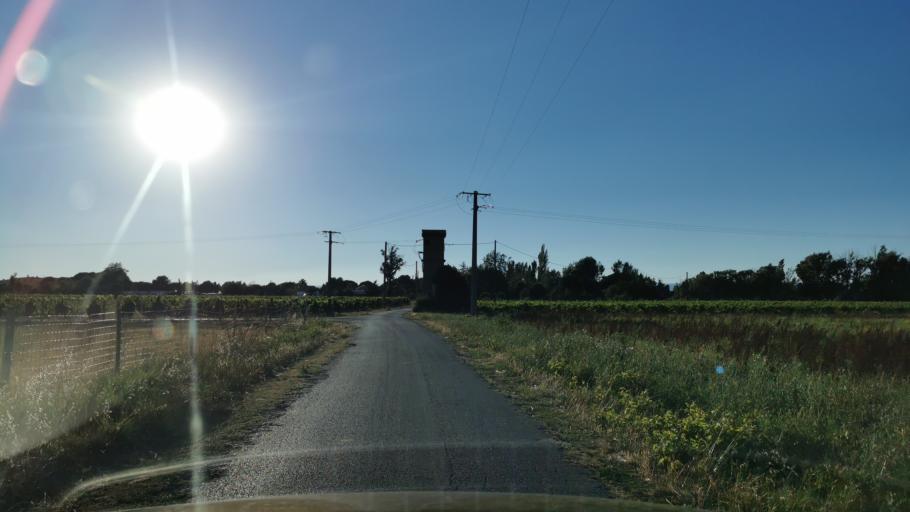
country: FR
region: Languedoc-Roussillon
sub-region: Departement de l'Aude
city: Coursan
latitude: 43.2654
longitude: 3.0205
